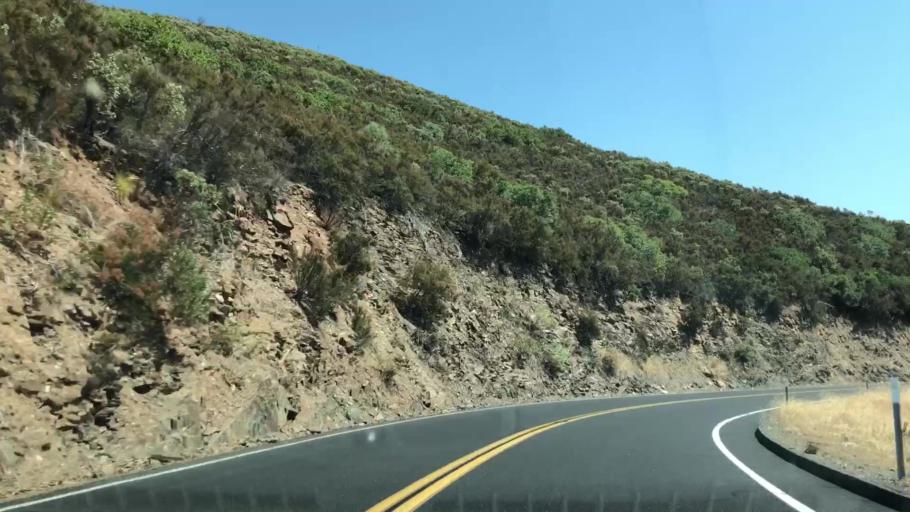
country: US
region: California
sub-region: Tuolumne County
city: Tuolumne City
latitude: 37.8200
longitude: -120.2763
